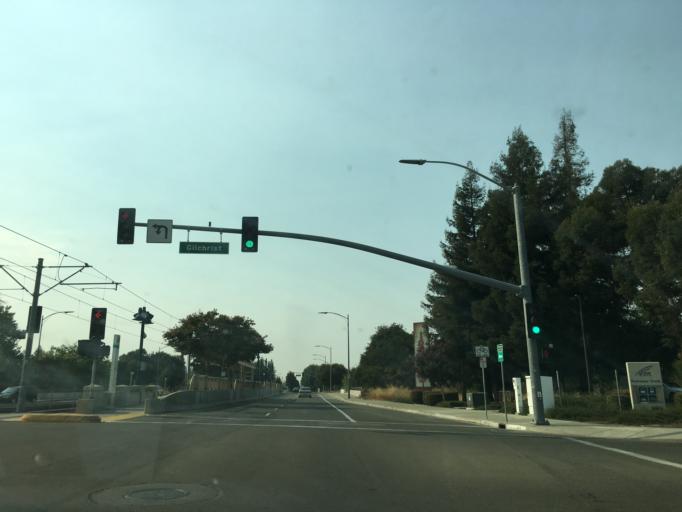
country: US
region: California
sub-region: Santa Clara County
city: Alum Rock
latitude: 37.3817
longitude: -121.8550
